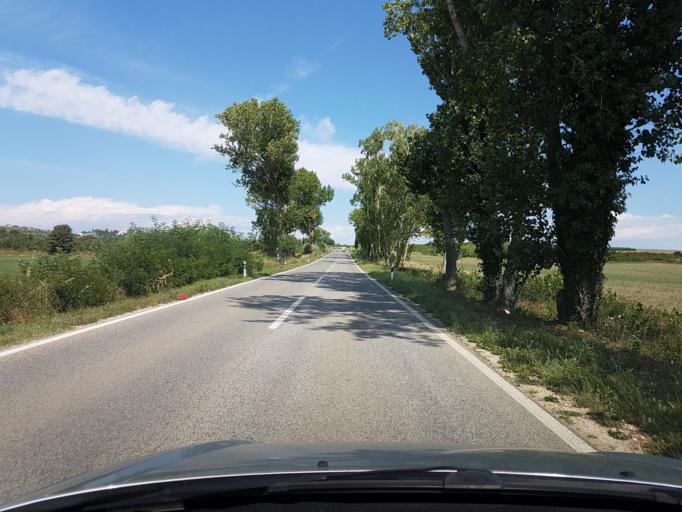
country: HR
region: Istarska
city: Buje
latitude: 45.4035
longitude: 13.6287
